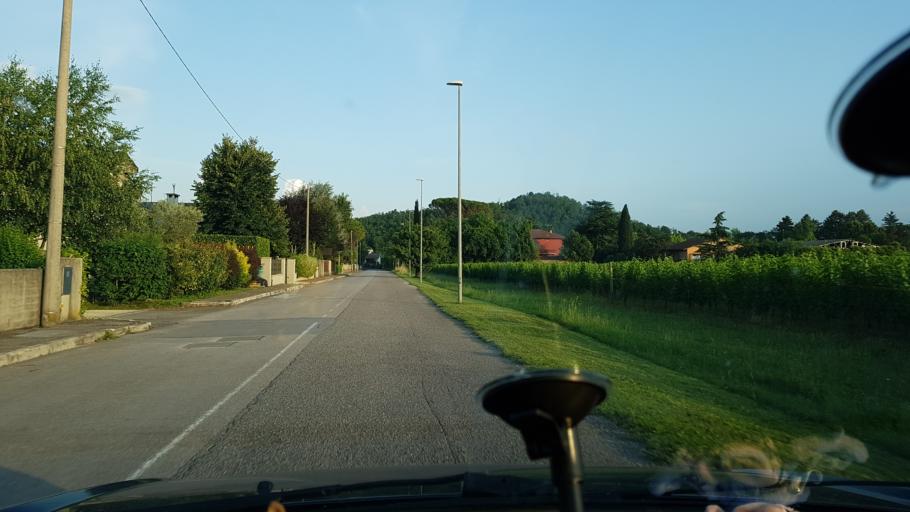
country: IT
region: Friuli Venezia Giulia
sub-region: Provincia di Gorizia
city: San Lorenzo Isontino
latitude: 45.9158
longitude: 13.5331
